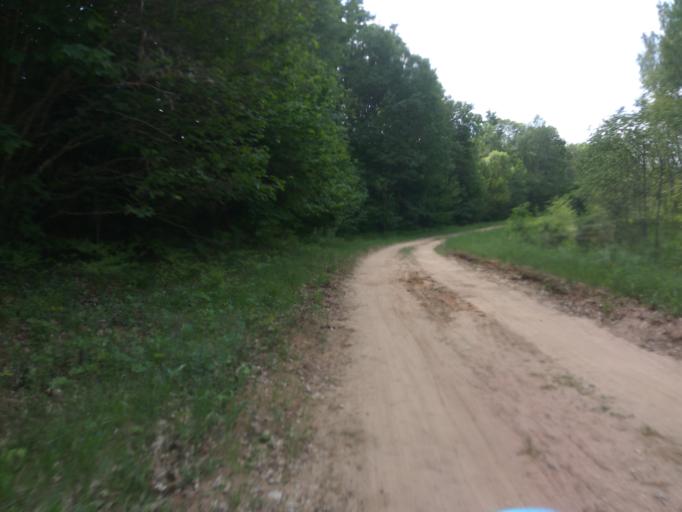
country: LV
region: Kuldigas Rajons
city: Kuldiga
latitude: 56.8815
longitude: 21.9720
